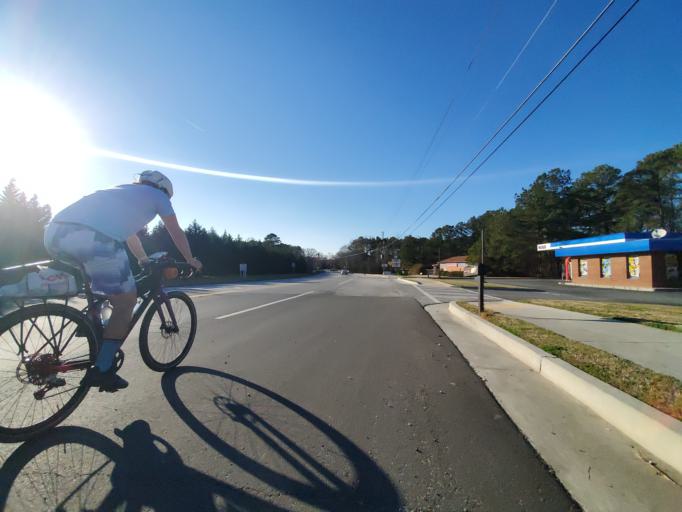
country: US
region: Georgia
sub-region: Gwinnett County
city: Lilburn
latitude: 33.8902
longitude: -84.1257
